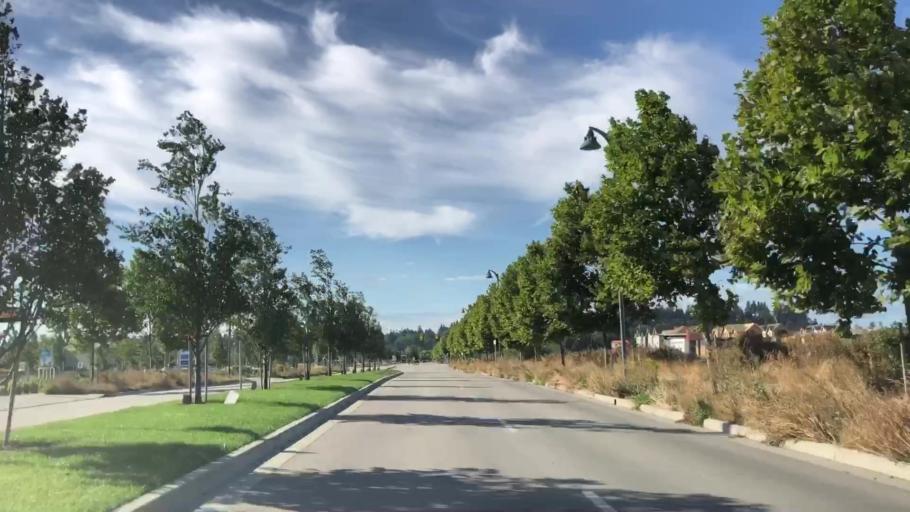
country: CA
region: British Columbia
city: Ladner
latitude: 49.0394
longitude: -123.0903
